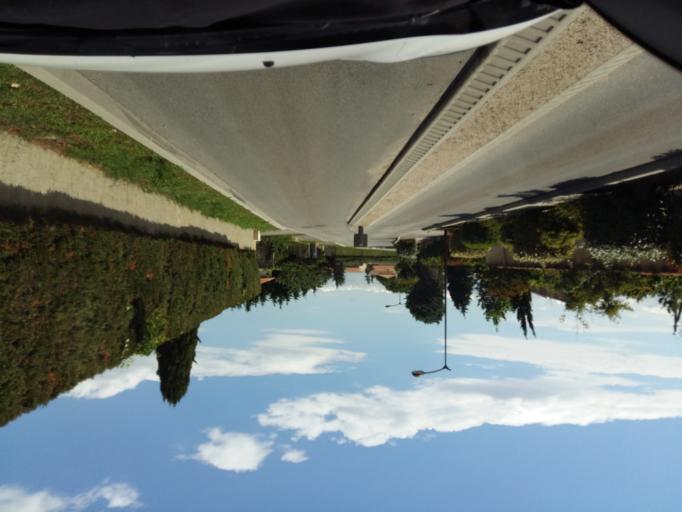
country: FR
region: Provence-Alpes-Cote d'Azur
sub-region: Departement du Vaucluse
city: Taillades
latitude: 43.8418
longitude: 5.0882
